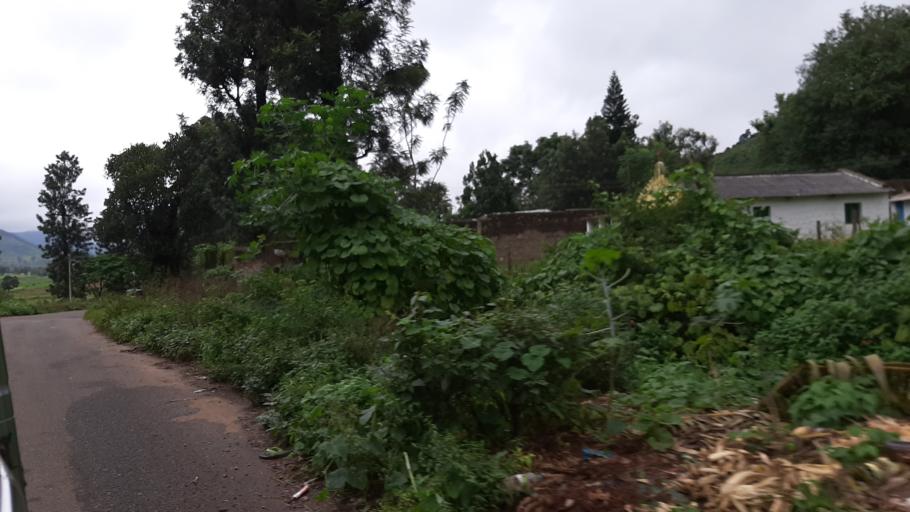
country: IN
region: Andhra Pradesh
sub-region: Vizianagaram District
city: Salur
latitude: 18.2927
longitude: 82.9196
